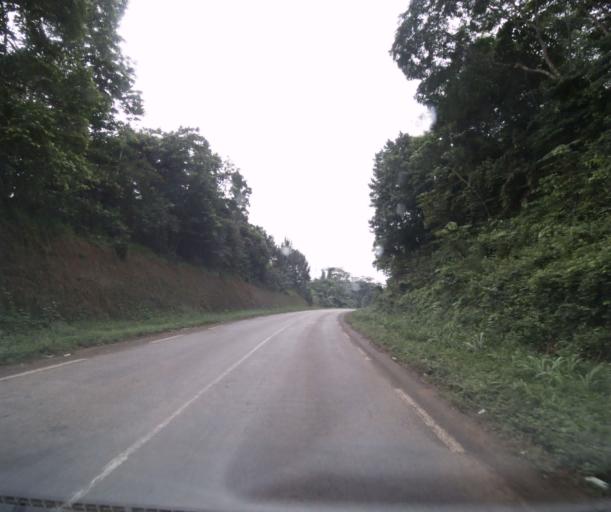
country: CM
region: Littoral
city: Edea
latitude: 3.8410
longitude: 10.4682
